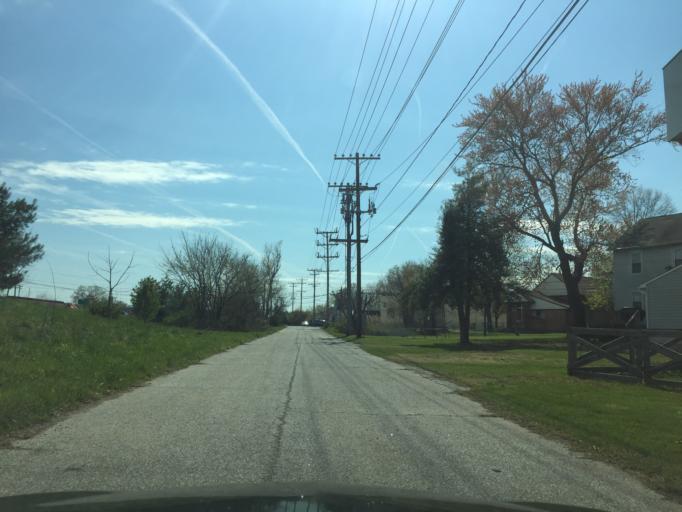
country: US
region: Maryland
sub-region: Baltimore County
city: Middle River
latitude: 39.3309
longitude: -76.4391
